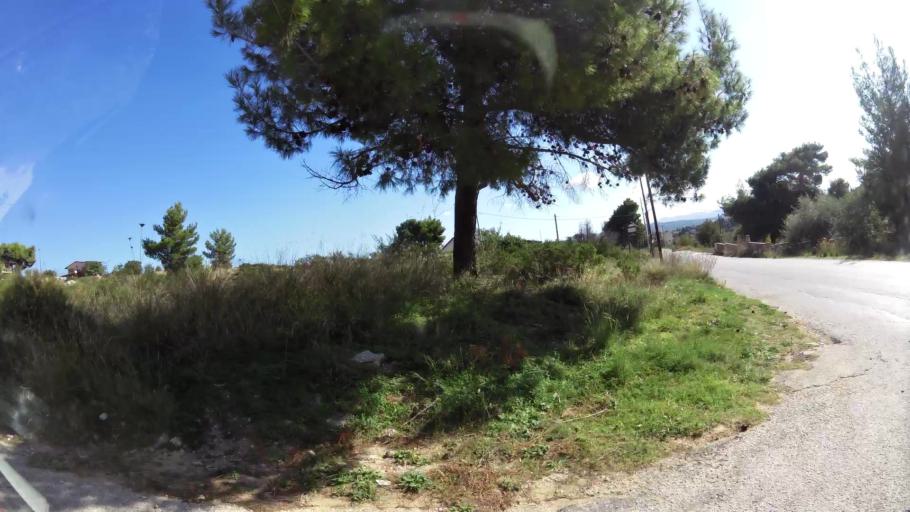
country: GR
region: Attica
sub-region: Nomarchia Anatolikis Attikis
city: Dioni
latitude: 38.0157
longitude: 23.9336
